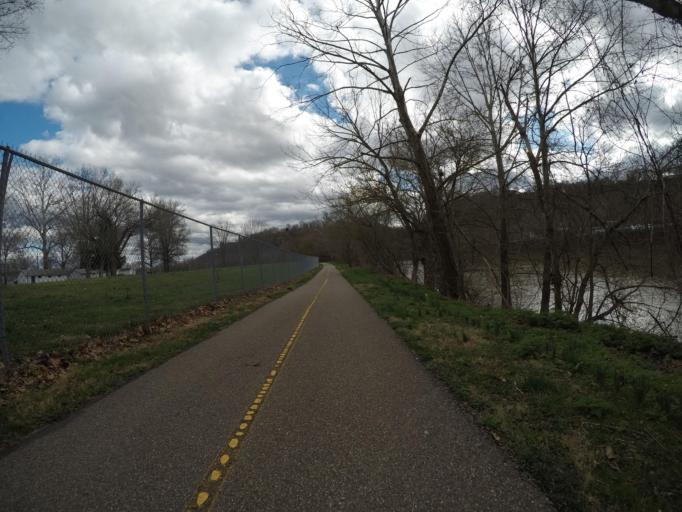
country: US
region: Ohio
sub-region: Washington County
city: Marietta
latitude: 39.4282
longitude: -81.4726
